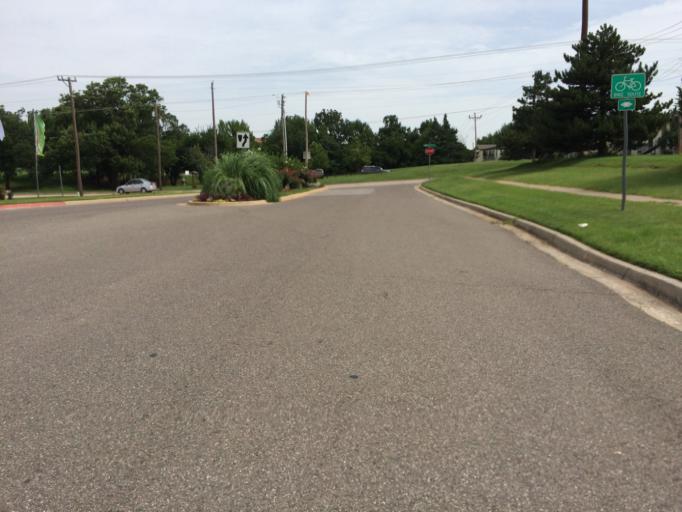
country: US
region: Oklahoma
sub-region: Cleveland County
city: Norman
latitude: 35.2032
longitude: -97.4161
